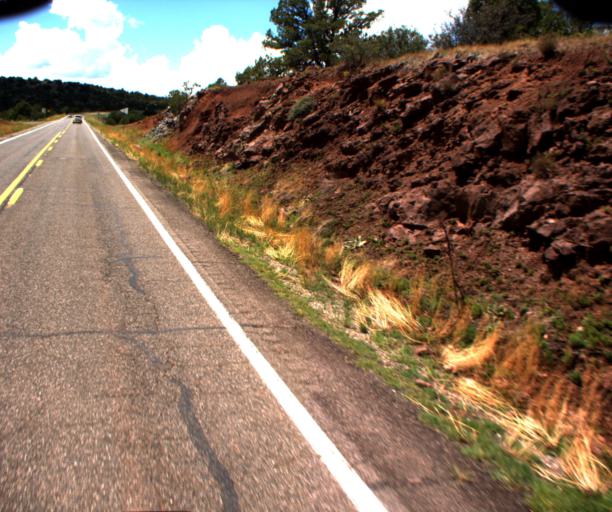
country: US
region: Arizona
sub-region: Gila County
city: Pine
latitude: 34.4861
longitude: -111.6153
